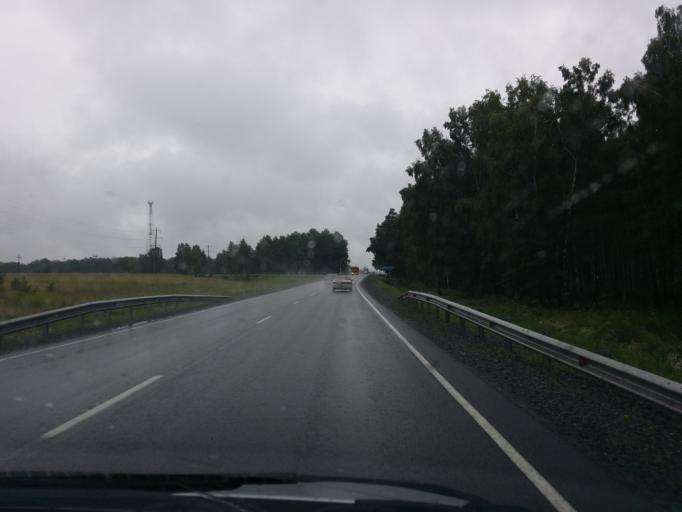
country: RU
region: Altai Krai
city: Bayunovskiye Klyuchi
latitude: 53.3488
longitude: 84.1346
